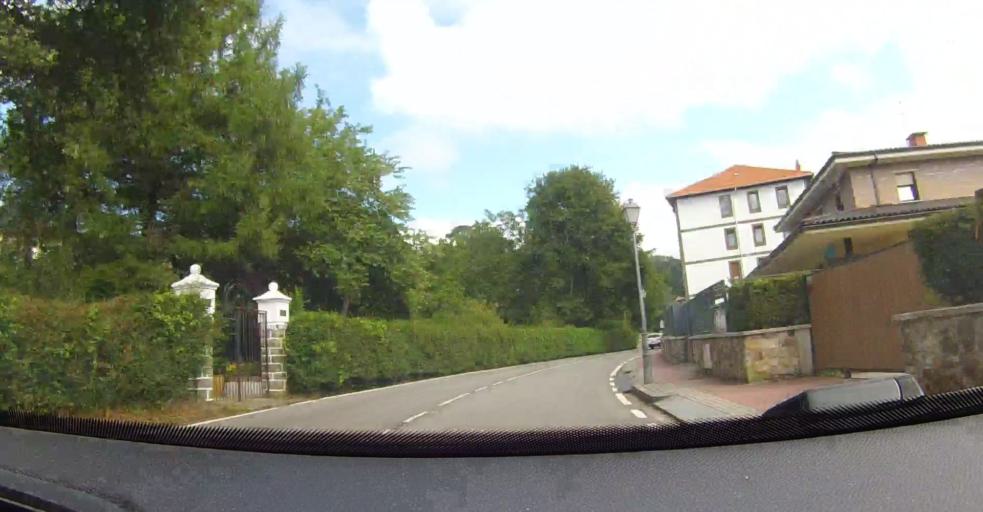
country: ES
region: Basque Country
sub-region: Bizkaia
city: Ibarrangelu
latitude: 43.3900
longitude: -2.6339
